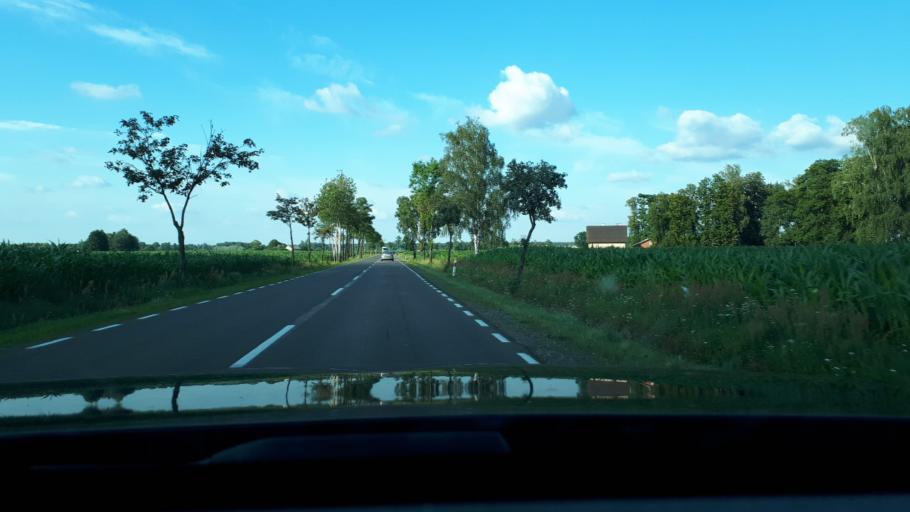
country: PL
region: Masovian Voivodeship
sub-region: Powiat plonski
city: Sochocin
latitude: 52.6570
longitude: 20.4348
